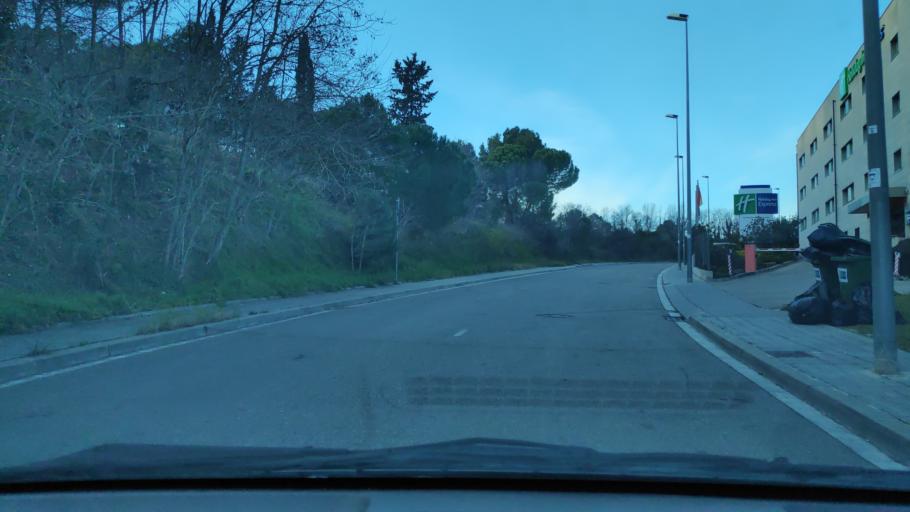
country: ES
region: Catalonia
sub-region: Provincia de Barcelona
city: Montmelo
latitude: 41.5702
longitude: 2.2654
